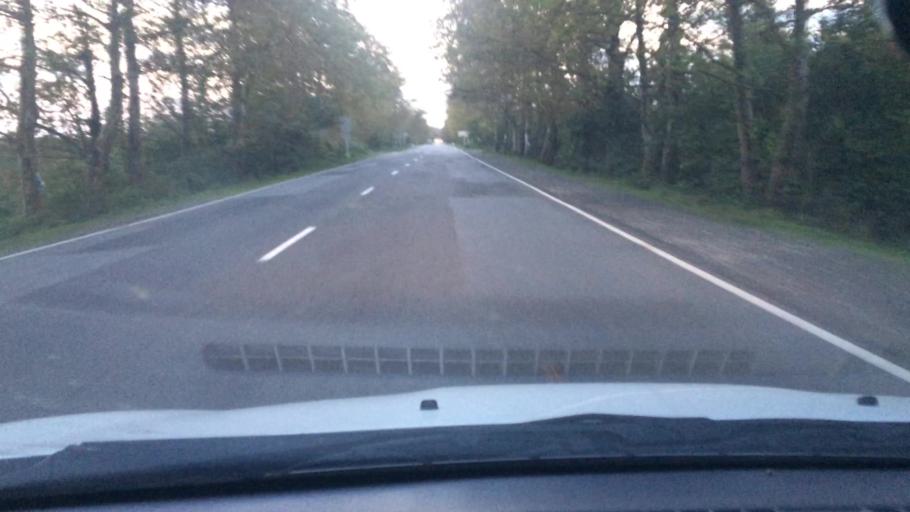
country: GE
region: Guria
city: Urek'i
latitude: 42.0147
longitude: 41.7723
